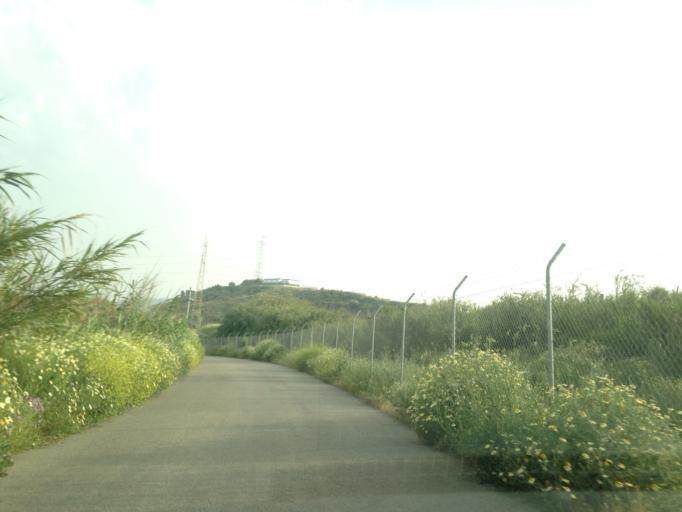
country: ES
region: Andalusia
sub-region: Provincia de Malaga
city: Estacion de Cartama
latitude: 36.7413
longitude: -4.5447
